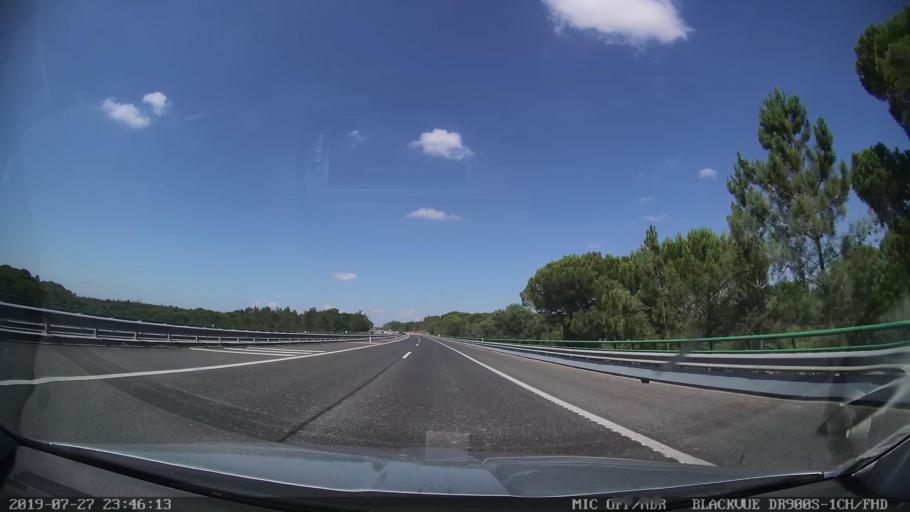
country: PT
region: Evora
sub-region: Vendas Novas
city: Vendas Novas
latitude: 38.6367
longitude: -8.4960
